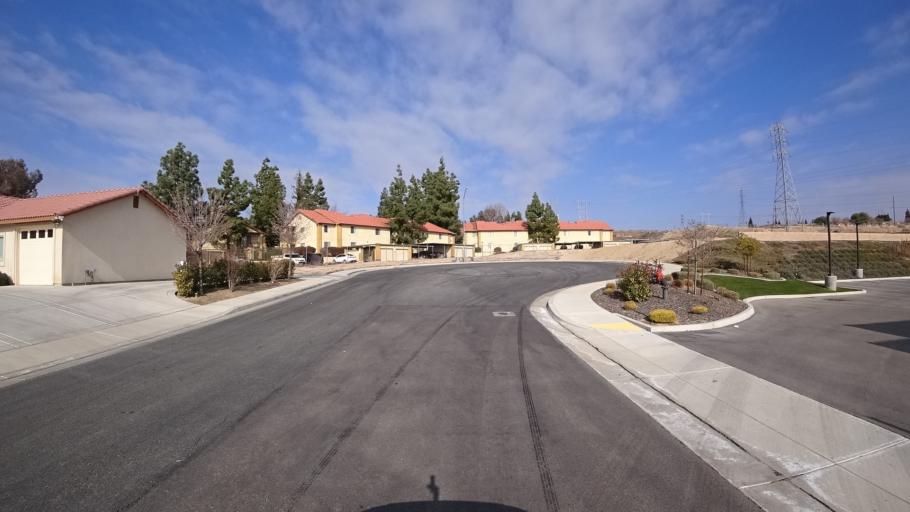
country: US
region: California
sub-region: Kern County
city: Bakersfield
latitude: 35.3952
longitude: -118.9256
